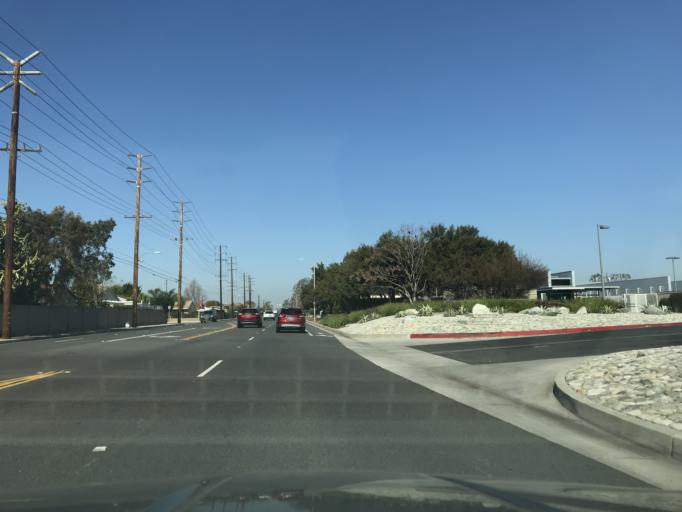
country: US
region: California
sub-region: Orange County
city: Fountain Valley
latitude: 33.6910
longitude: -117.9454
